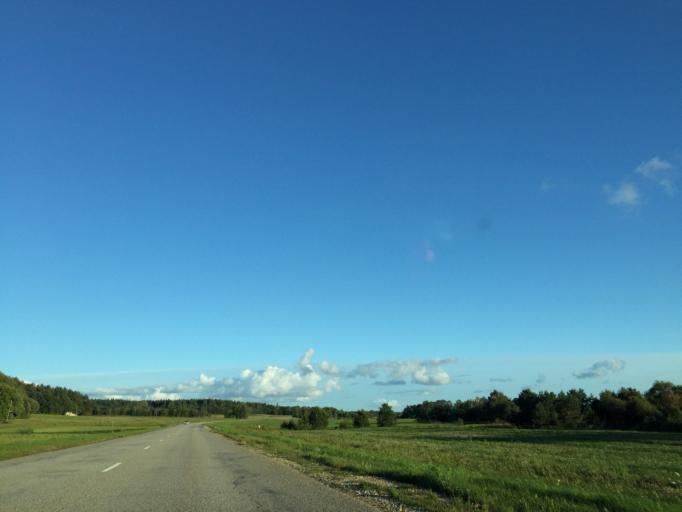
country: LV
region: Kuldigas Rajons
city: Kuldiga
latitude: 56.9296
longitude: 22.0442
